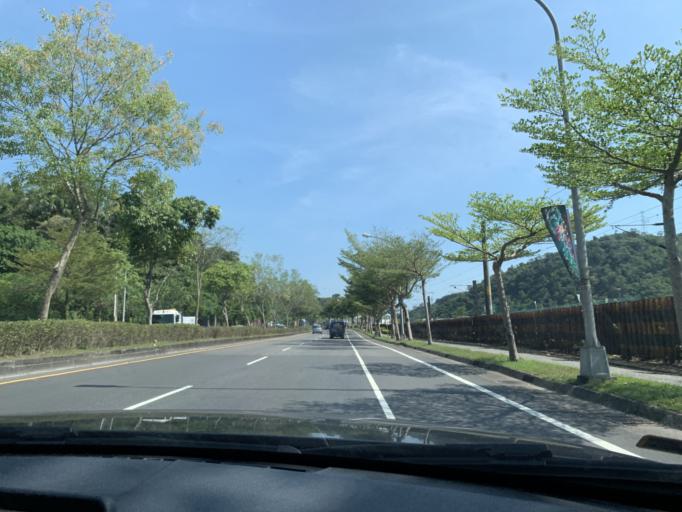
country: TW
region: Taiwan
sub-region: Yilan
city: Yilan
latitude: 24.5999
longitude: 121.8345
